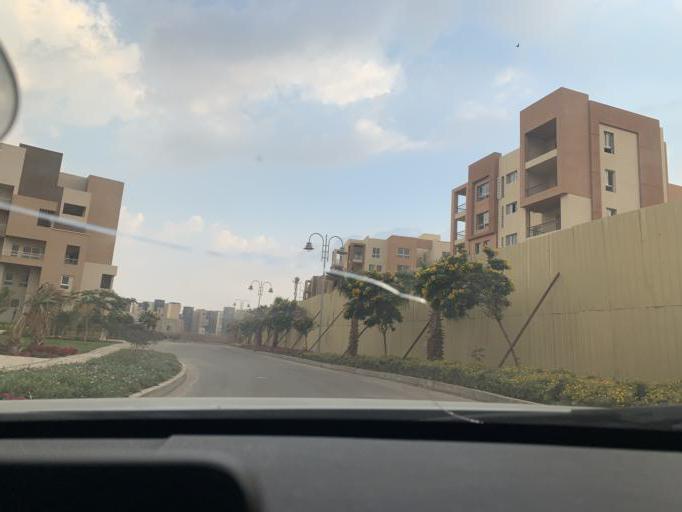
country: EG
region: Muhafazat al Qalyubiyah
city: Al Khankah
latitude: 30.1024
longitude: 31.6502
